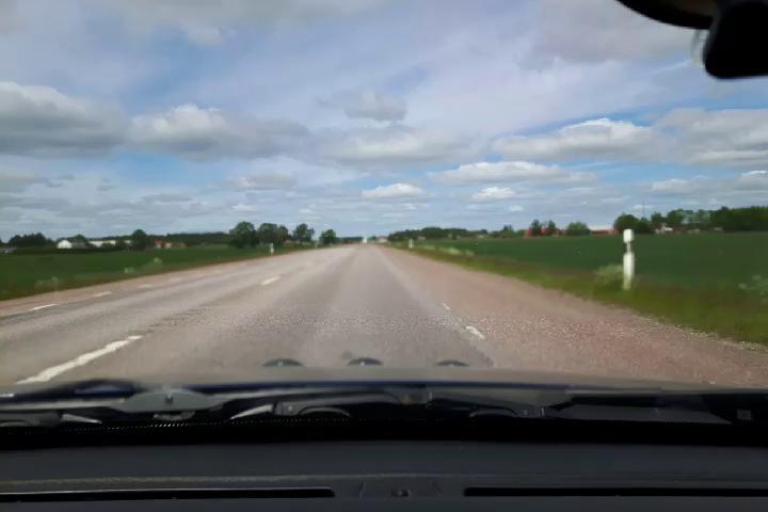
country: SE
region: Uppsala
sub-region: Uppsala Kommun
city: Gamla Uppsala
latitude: 59.9228
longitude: 17.6015
